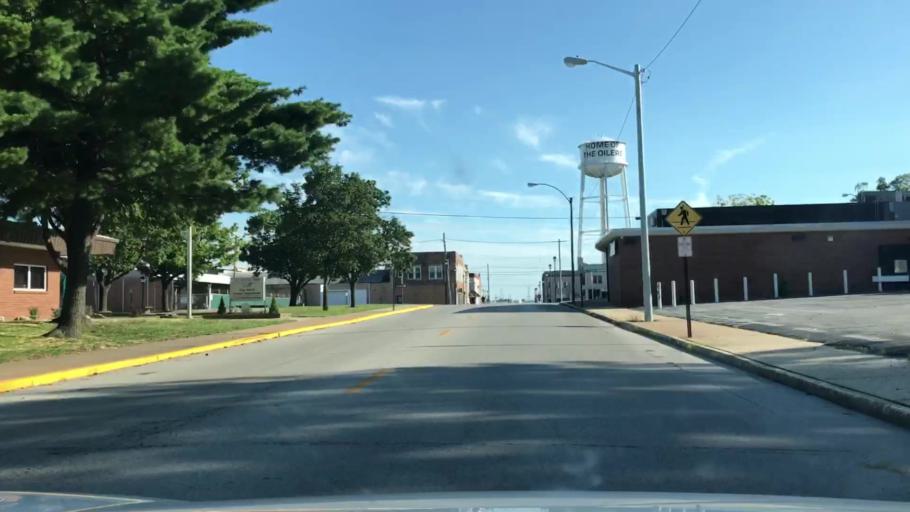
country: US
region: Illinois
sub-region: Madison County
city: Wood River
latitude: 38.8626
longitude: -90.0983
